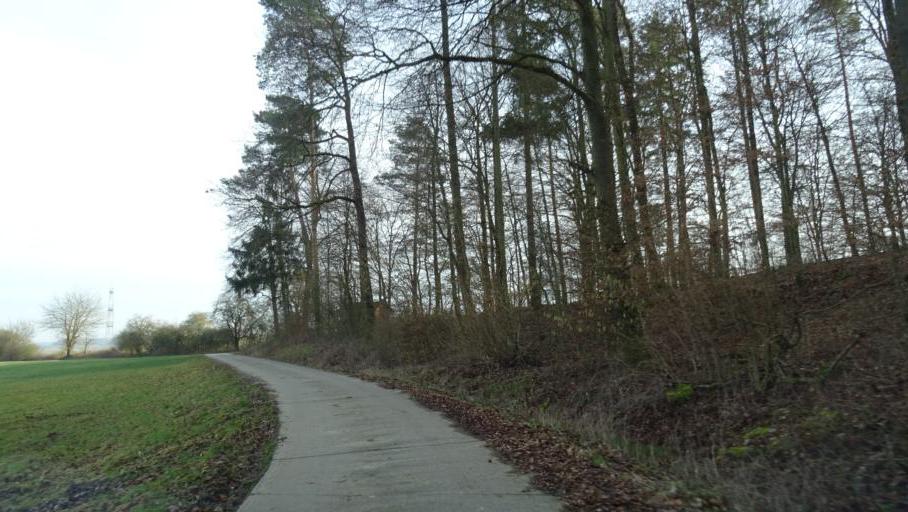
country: DE
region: Baden-Wuerttemberg
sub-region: Karlsruhe Region
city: Mosbach
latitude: 49.3527
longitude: 9.1982
